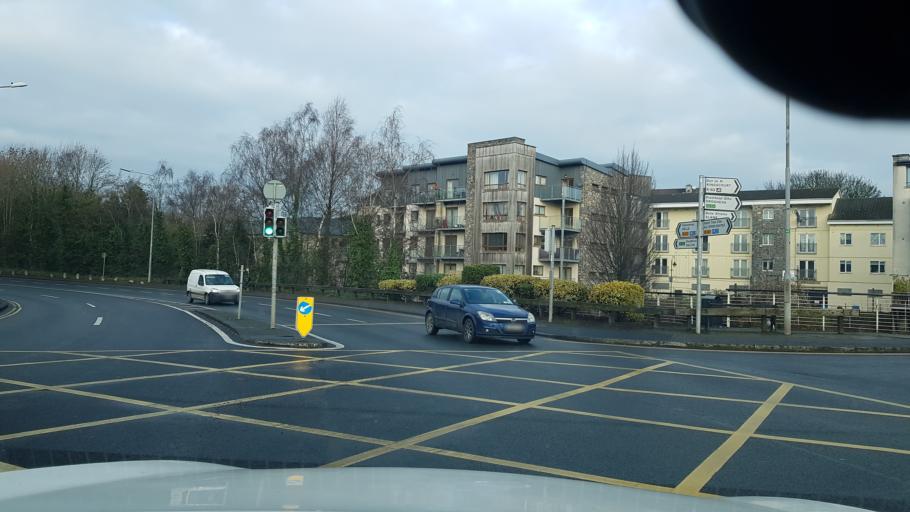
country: IE
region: Leinster
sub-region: An Mhi
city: Navan
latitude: 53.6545
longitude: -6.6824
